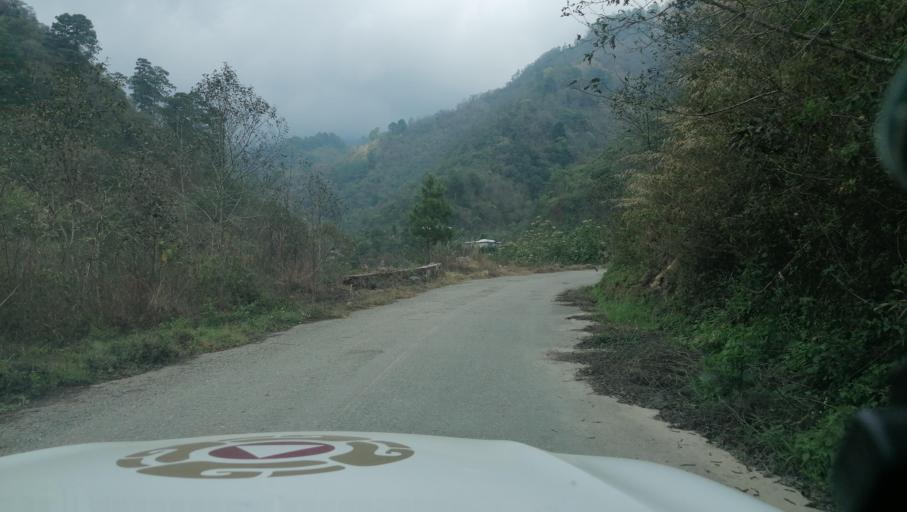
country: GT
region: San Marcos
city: Tacana
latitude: 15.2217
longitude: -92.2000
